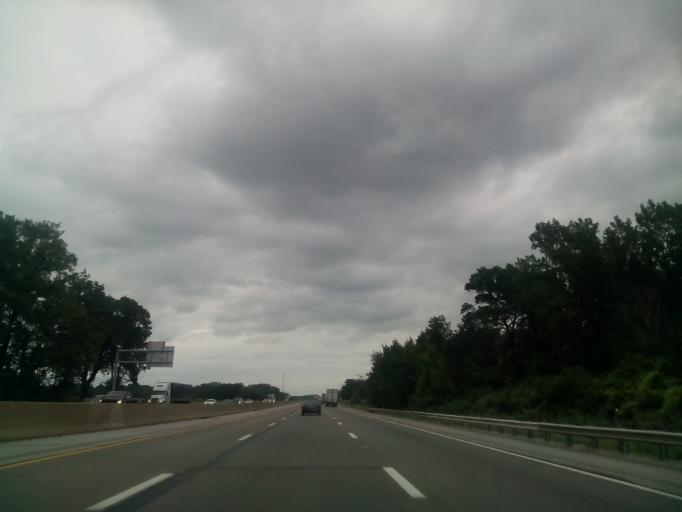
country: US
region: Ohio
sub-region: Erie County
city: Milan
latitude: 41.3237
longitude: -82.5681
